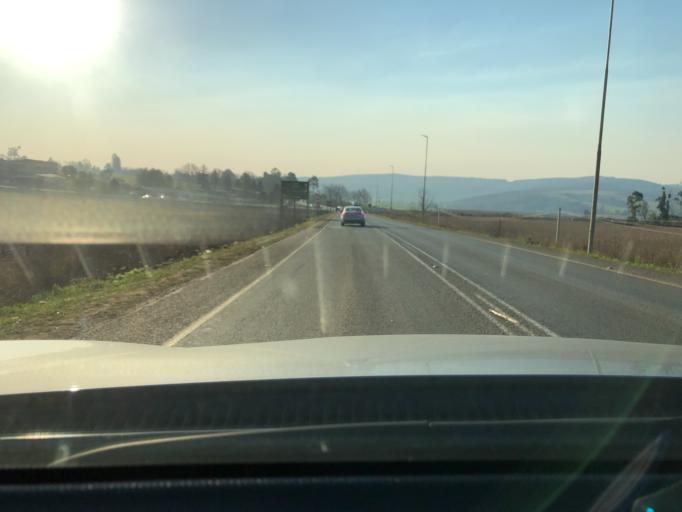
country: ZA
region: KwaZulu-Natal
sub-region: Sisonke District Municipality
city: Ixopo
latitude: -30.1475
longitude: 30.0730
